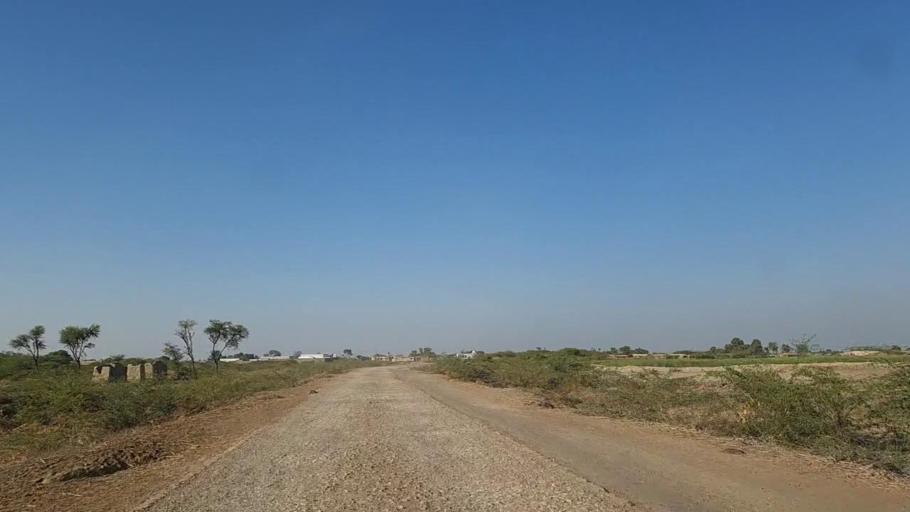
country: PK
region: Sindh
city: Samaro
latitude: 25.3608
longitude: 69.3751
